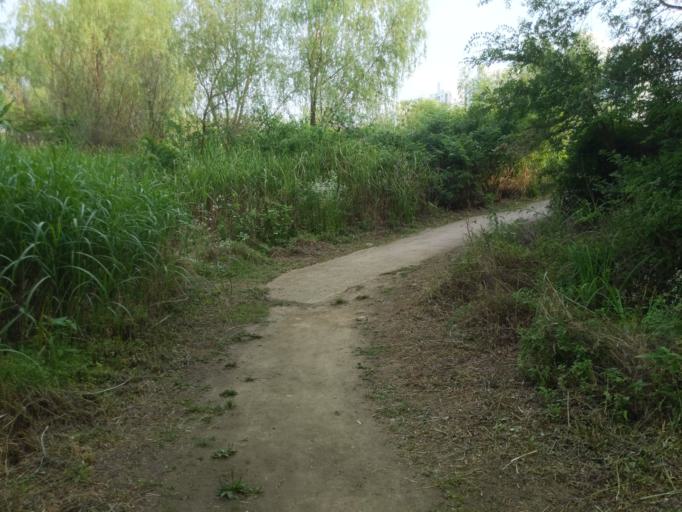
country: KR
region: Gyeonggi-do
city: Kwangmyong
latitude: 37.5373
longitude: 126.9054
